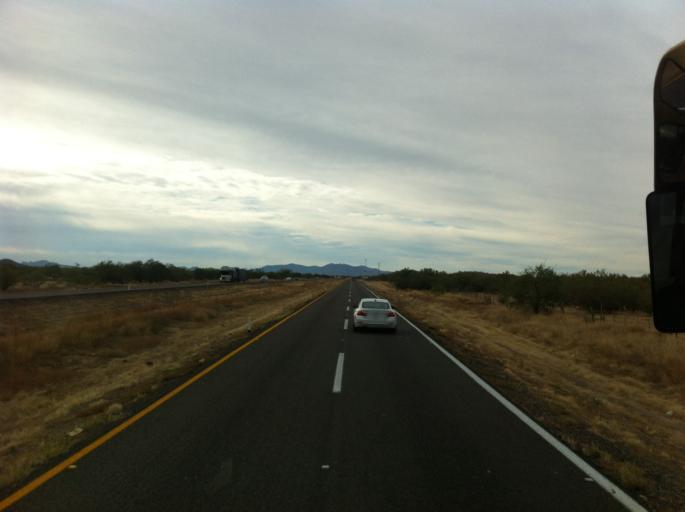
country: MX
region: Sonora
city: Hermosillo
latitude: 28.8220
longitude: -110.9583
